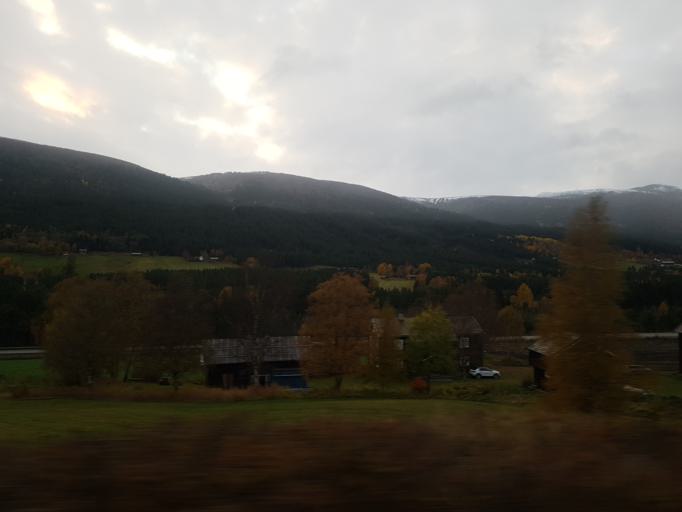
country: NO
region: Oppland
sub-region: Dovre
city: Dovre
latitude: 61.9940
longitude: 9.2335
